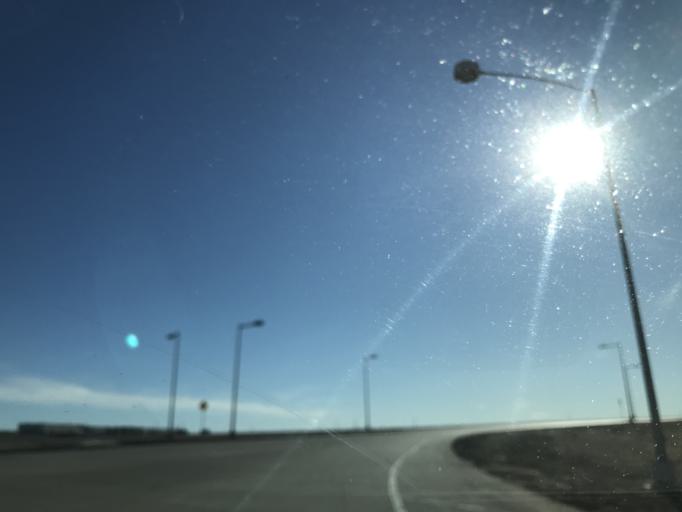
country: US
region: Colorado
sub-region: Weld County
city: Lochbuie
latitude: 39.8448
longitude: -104.6714
